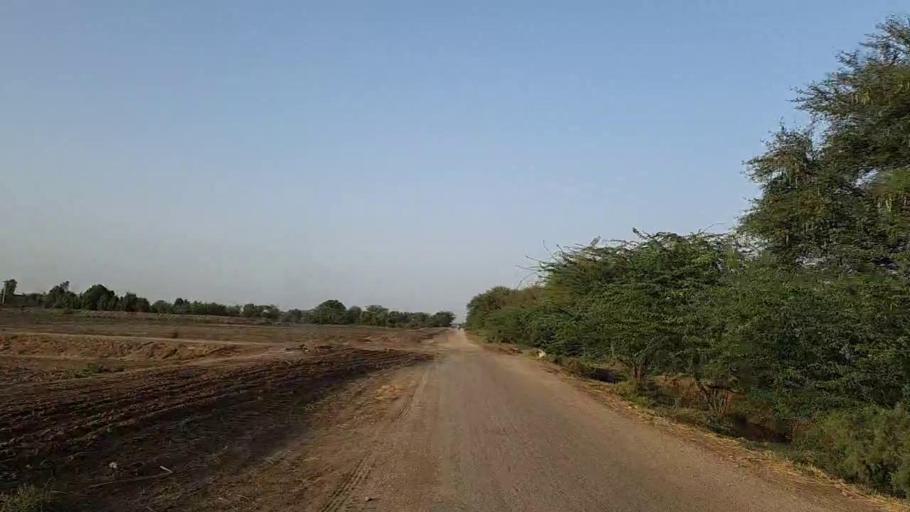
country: PK
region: Sindh
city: Jati
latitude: 24.4168
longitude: 68.1901
